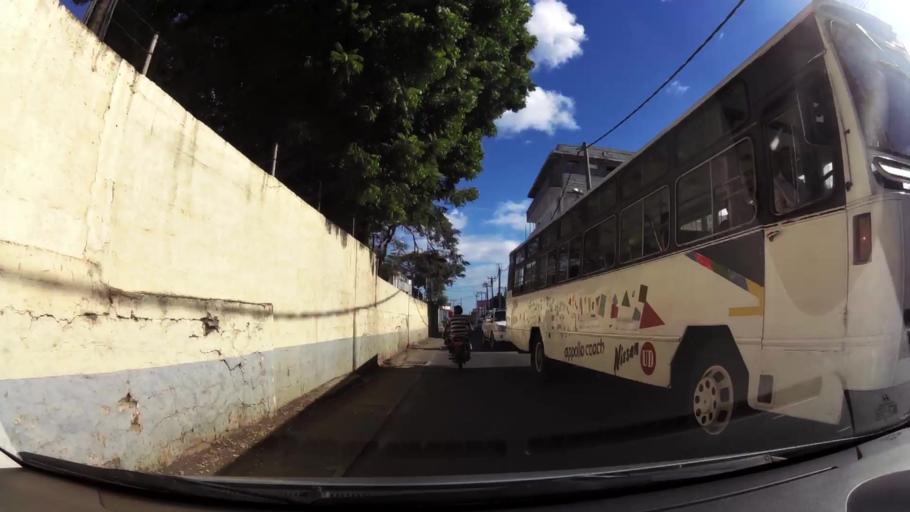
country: MU
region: Pamplemousses
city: Le Hochet
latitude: -20.1435
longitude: 57.5128
